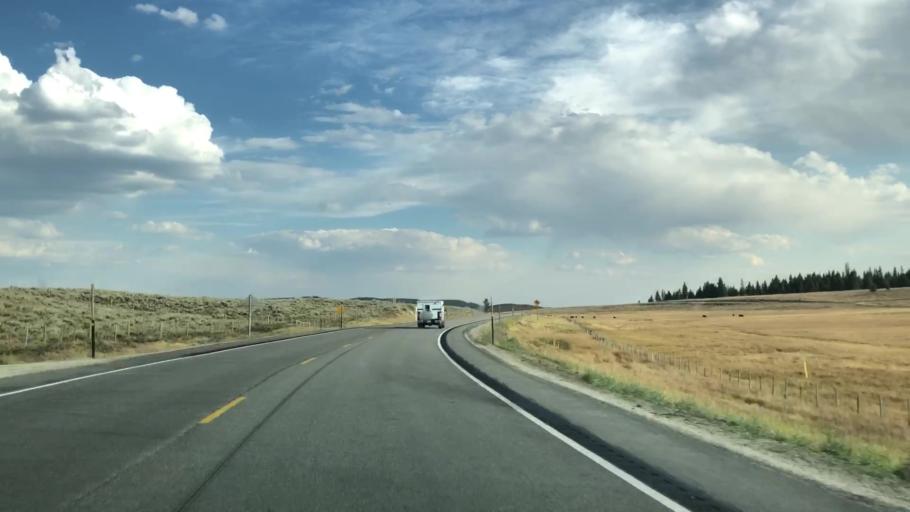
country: US
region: Wyoming
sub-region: Sublette County
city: Pinedale
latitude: 43.1302
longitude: -110.1916
